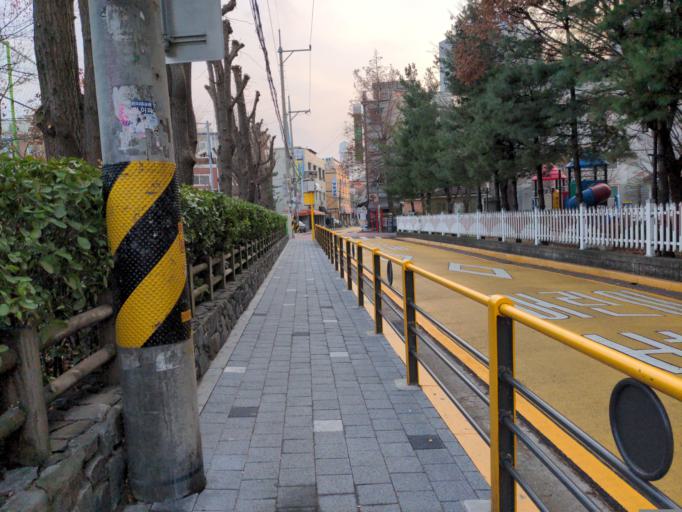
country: KR
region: Seoul
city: Seoul
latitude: 37.5392
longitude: 127.0578
